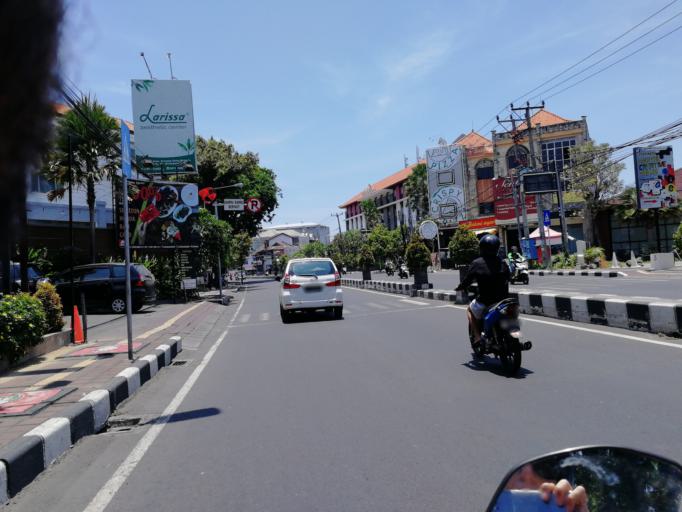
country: ID
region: Bali
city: Karyadharma
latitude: -8.6809
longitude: 115.2019
